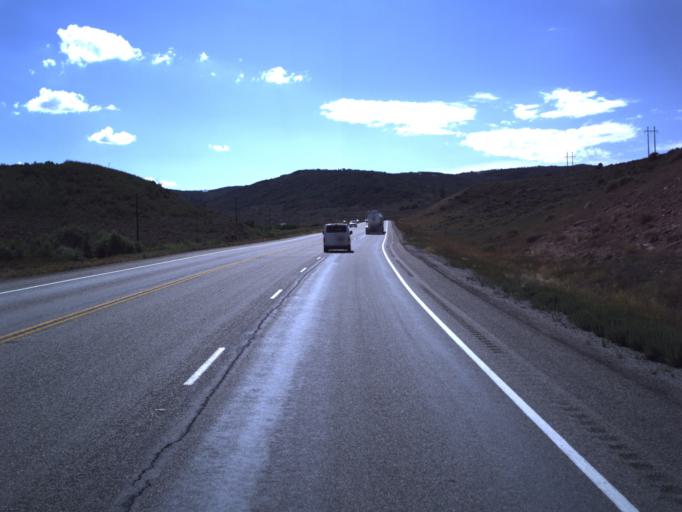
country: US
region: Utah
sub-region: Summit County
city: Francis
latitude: 40.2004
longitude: -110.9910
